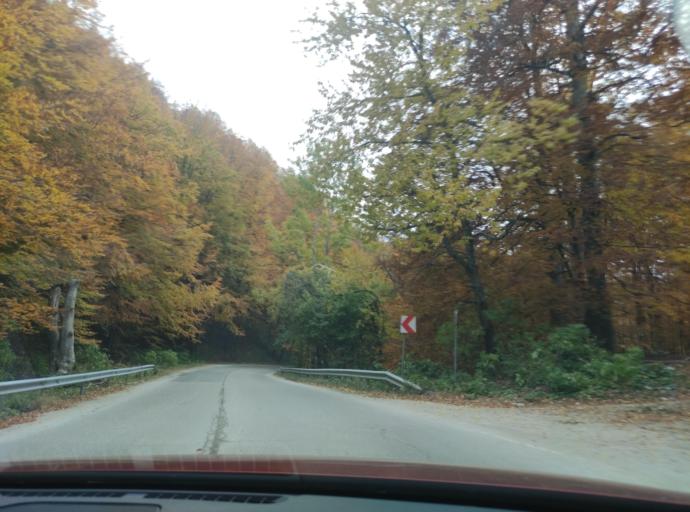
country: BG
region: Montana
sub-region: Obshtina Berkovitsa
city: Berkovitsa
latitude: 43.1348
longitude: 23.1504
